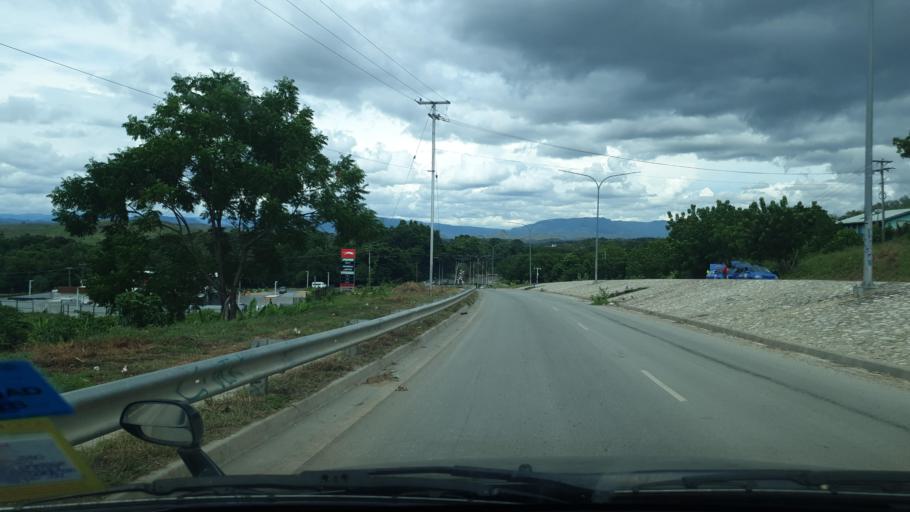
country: PG
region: National Capital
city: Port Moresby
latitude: -9.4088
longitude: 147.1624
